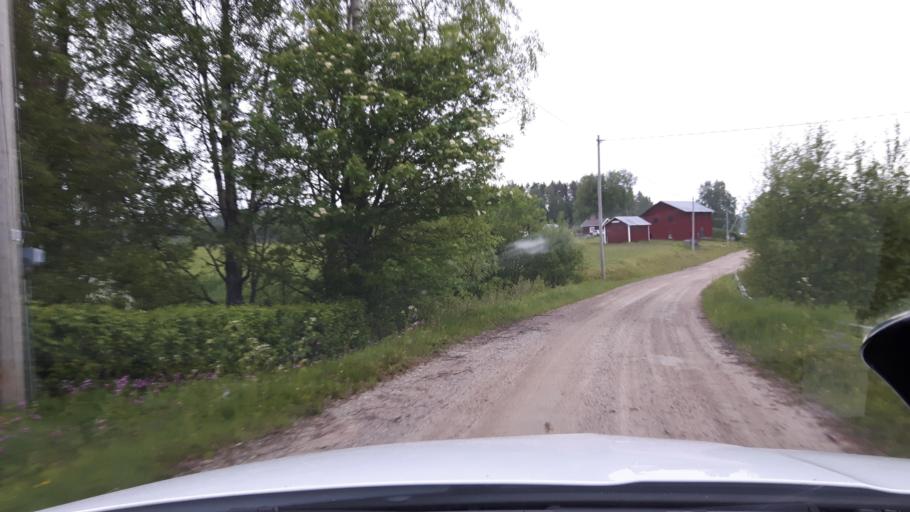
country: SE
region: Vaesternorrland
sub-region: Ange Kommun
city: Ange
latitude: 62.1469
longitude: 15.6672
